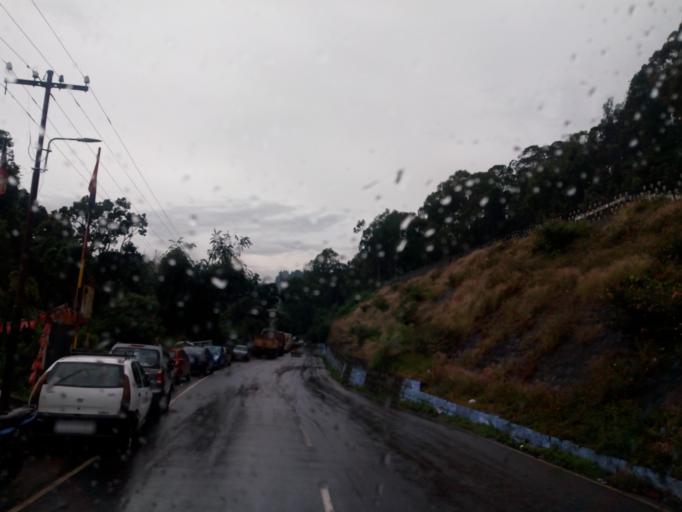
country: IN
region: Tamil Nadu
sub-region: Nilgiri
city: Wellington
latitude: 11.3430
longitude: 76.7994
